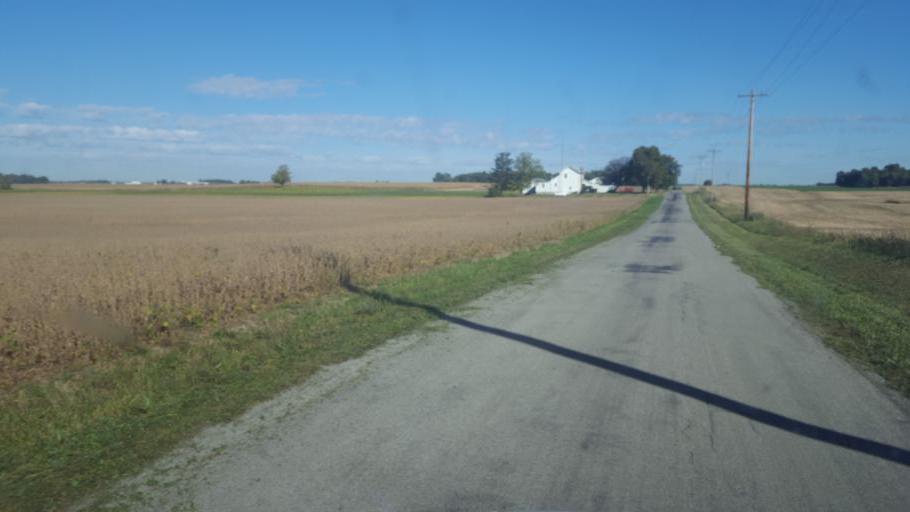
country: US
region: Ohio
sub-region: Wyandot County
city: Upper Sandusky
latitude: 40.7862
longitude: -83.2173
